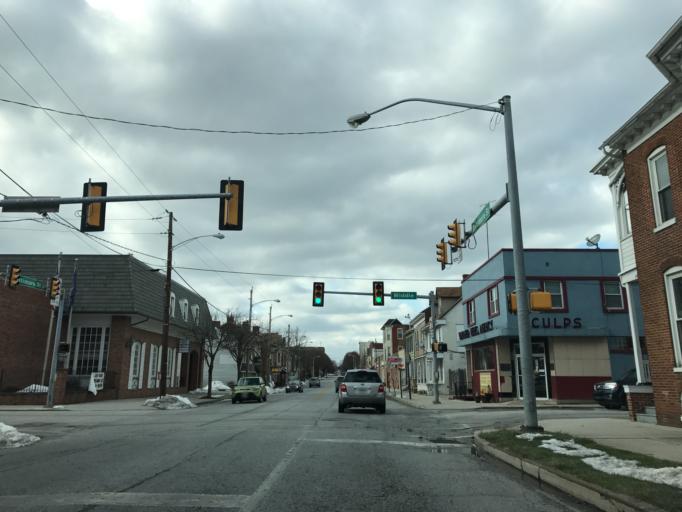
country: US
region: Pennsylvania
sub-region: York County
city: Hanover
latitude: 39.7982
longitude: -76.9808
